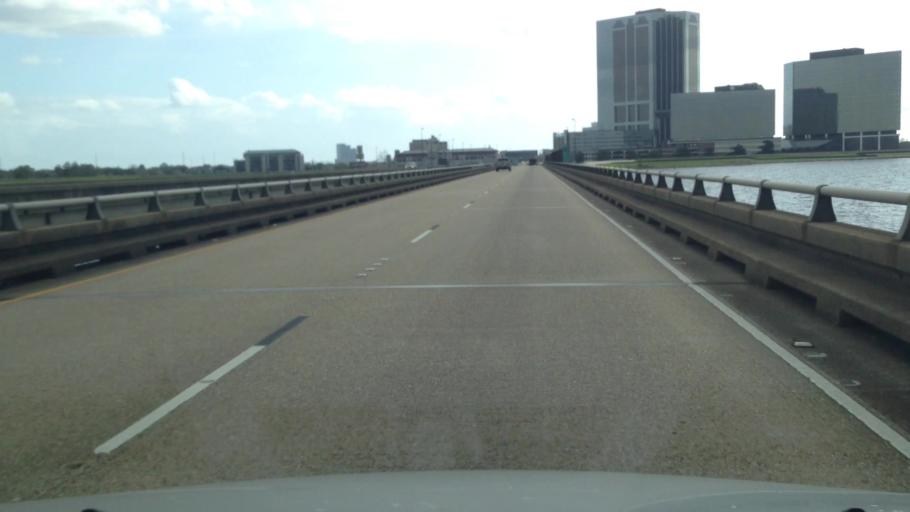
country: US
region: Louisiana
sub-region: Jefferson Parish
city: Metairie
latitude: 30.0255
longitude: -90.1535
